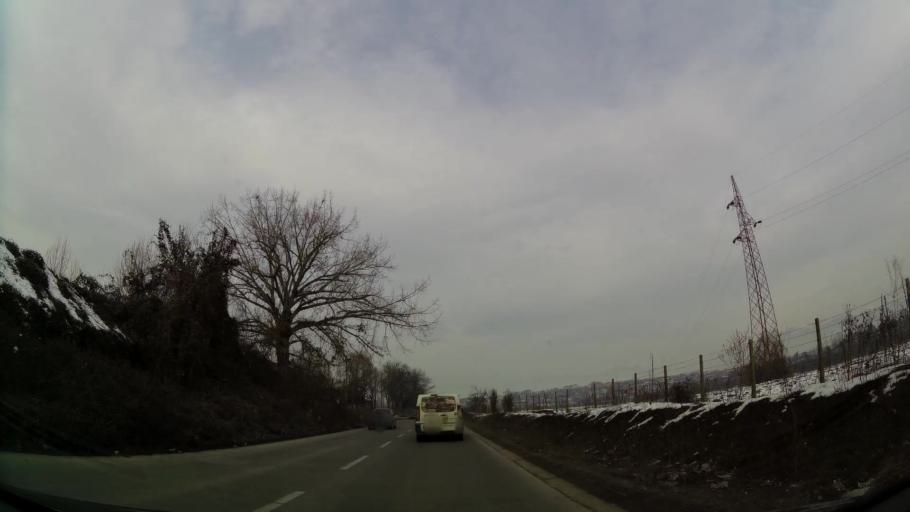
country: MK
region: Suto Orizari
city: Suto Orizare
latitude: 42.0212
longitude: 21.4098
